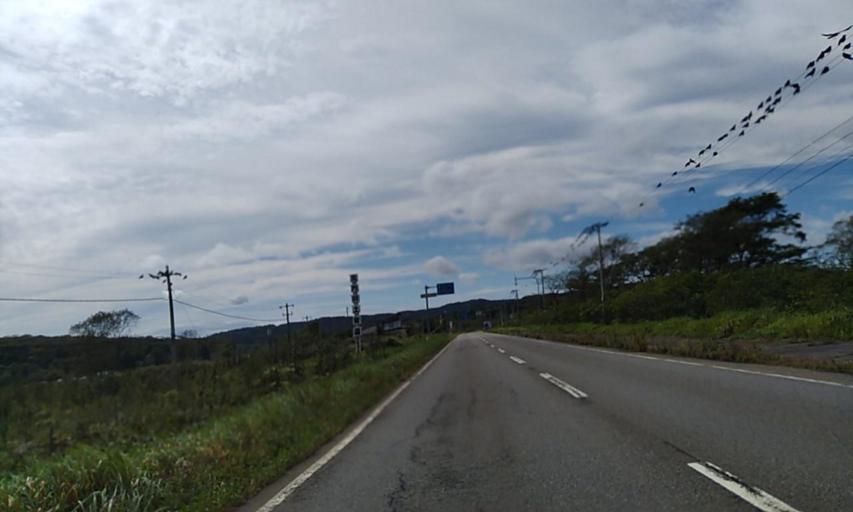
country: JP
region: Hokkaido
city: Kushiro
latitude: 42.8514
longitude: 143.8580
